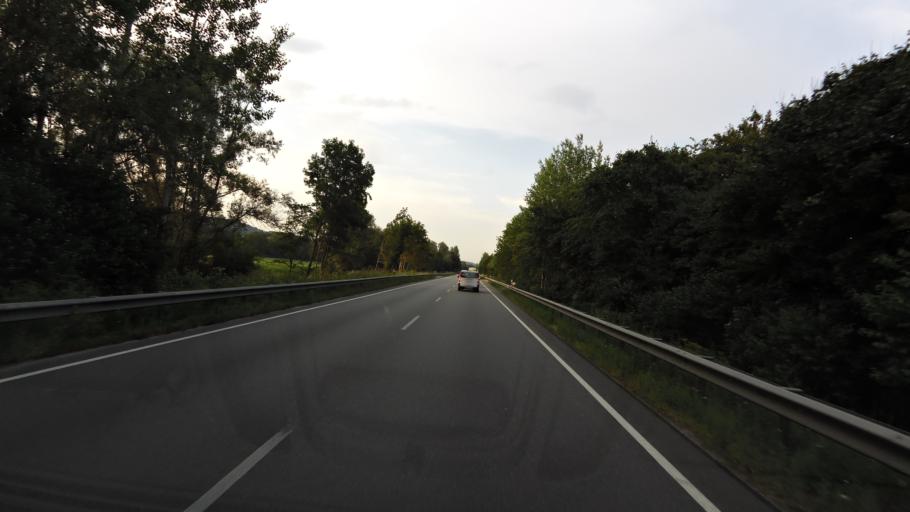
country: DE
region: Bavaria
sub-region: Lower Bavaria
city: Kirchdorf am Inn
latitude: 48.2425
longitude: 12.9894
